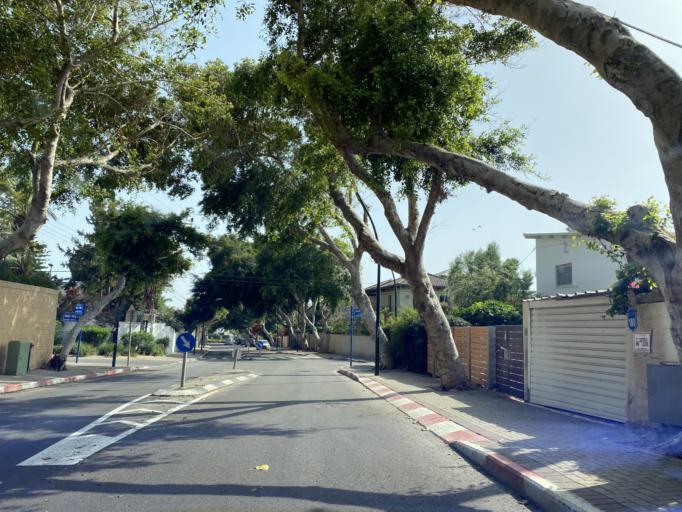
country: IL
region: Tel Aviv
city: Herzliya Pituah
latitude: 32.1701
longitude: 34.8065
